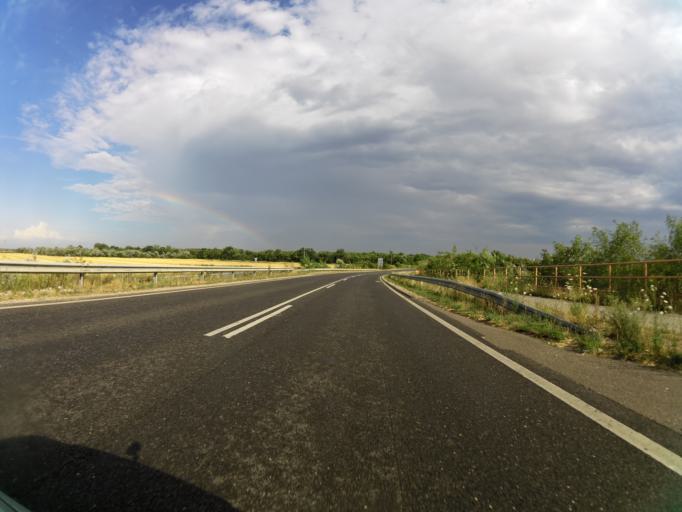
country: HU
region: Csongrad
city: Szeged
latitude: 46.2919
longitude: 20.1363
